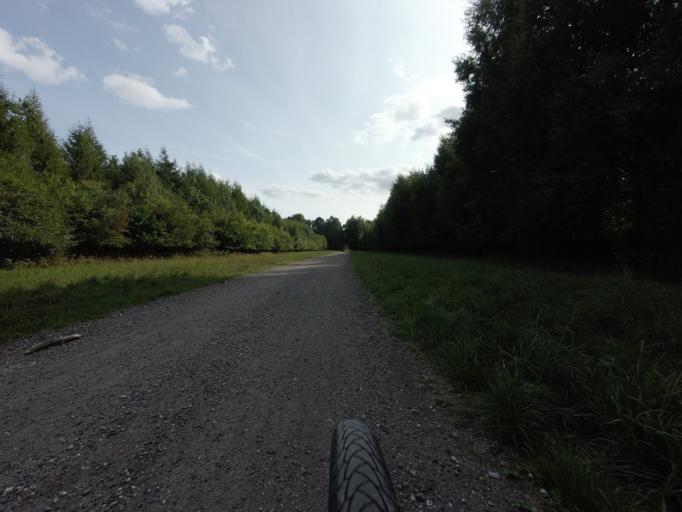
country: DK
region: Zealand
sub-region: Vordingborg Kommune
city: Praesto
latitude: 55.1540
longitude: 12.0947
